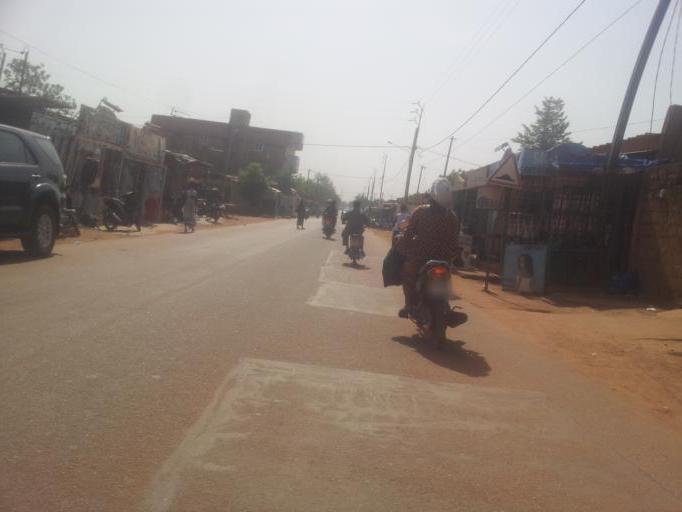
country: BF
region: Centre
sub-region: Kadiogo Province
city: Ouagadougou
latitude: 12.3782
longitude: -1.5389
